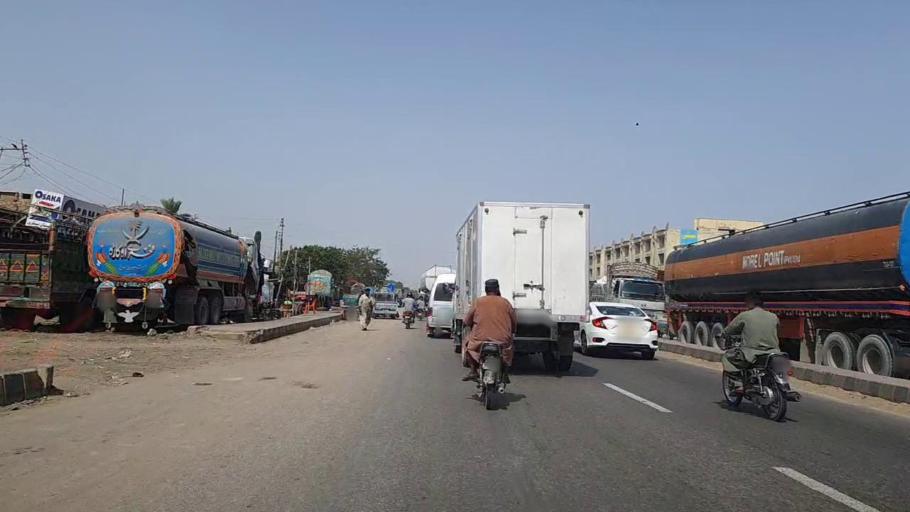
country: PK
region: Sindh
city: Malir Cantonment
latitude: 24.8563
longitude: 67.2595
